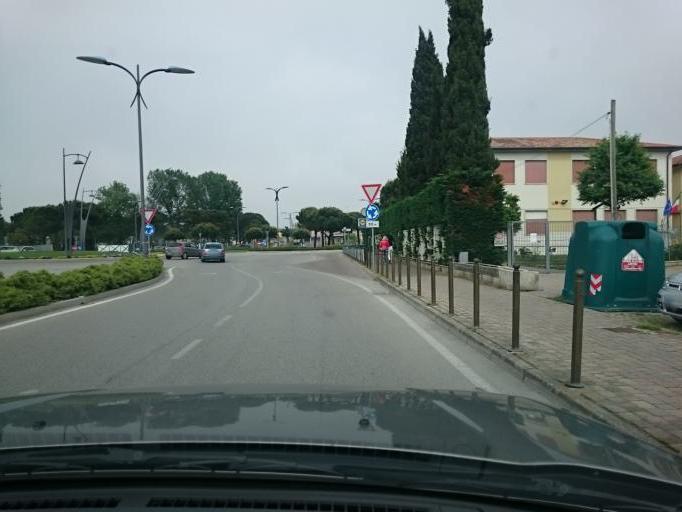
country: IT
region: Veneto
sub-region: Provincia di Venezia
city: Chioggia
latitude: 45.1962
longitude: 12.2829
